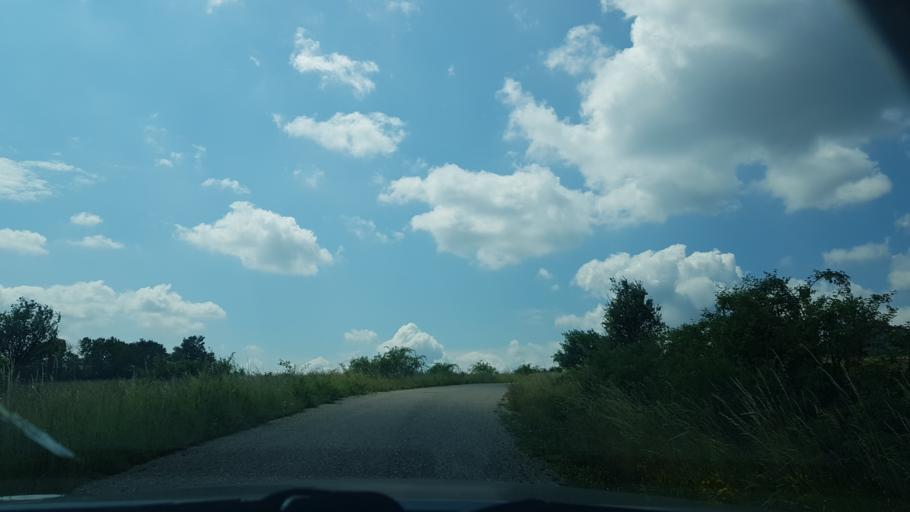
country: HU
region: Borsod-Abauj-Zemplen
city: Gonc
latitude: 48.5339
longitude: 21.4764
